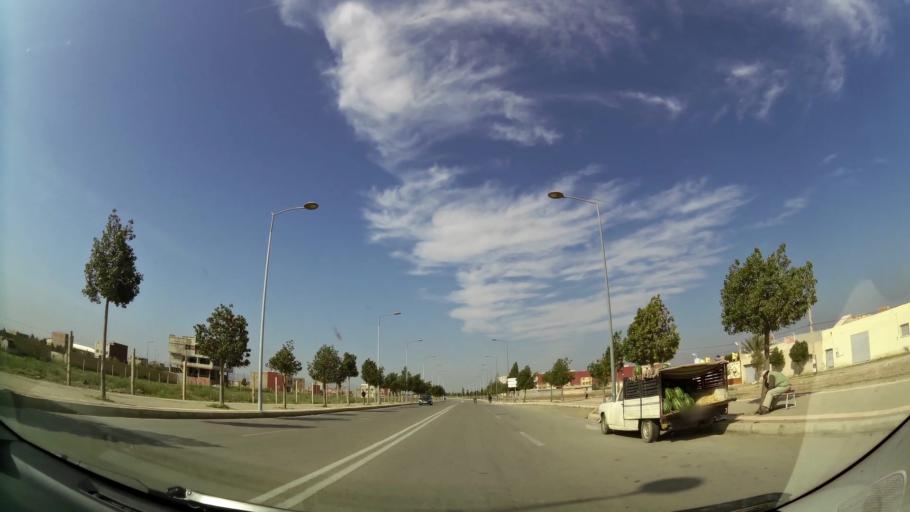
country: MA
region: Oriental
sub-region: Oujda-Angad
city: Oujda
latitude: 34.7129
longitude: -1.8866
